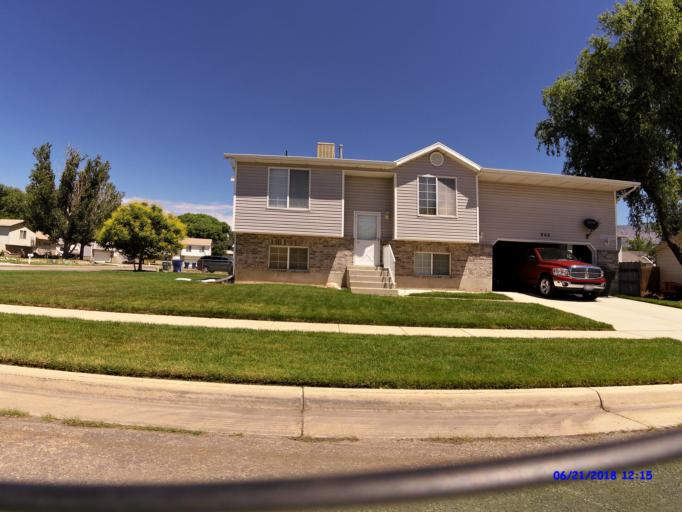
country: US
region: Utah
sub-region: Weber County
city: Harrisville
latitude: 41.2846
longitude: -112.0028
